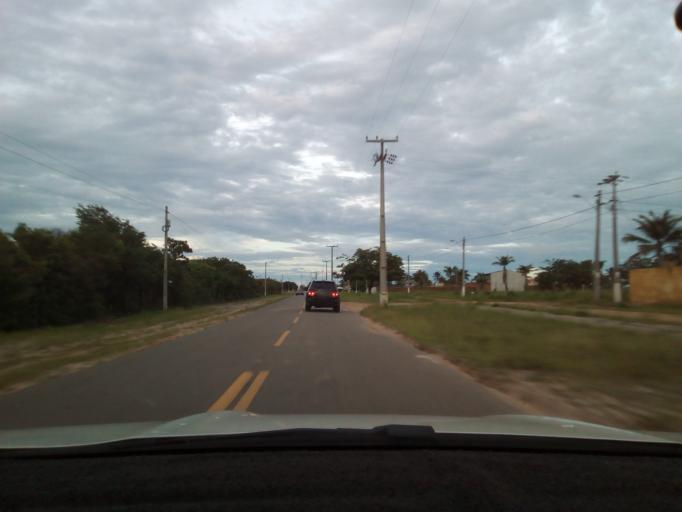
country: BR
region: Ceara
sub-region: Beberibe
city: Beberibe
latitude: -4.1859
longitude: -38.1096
